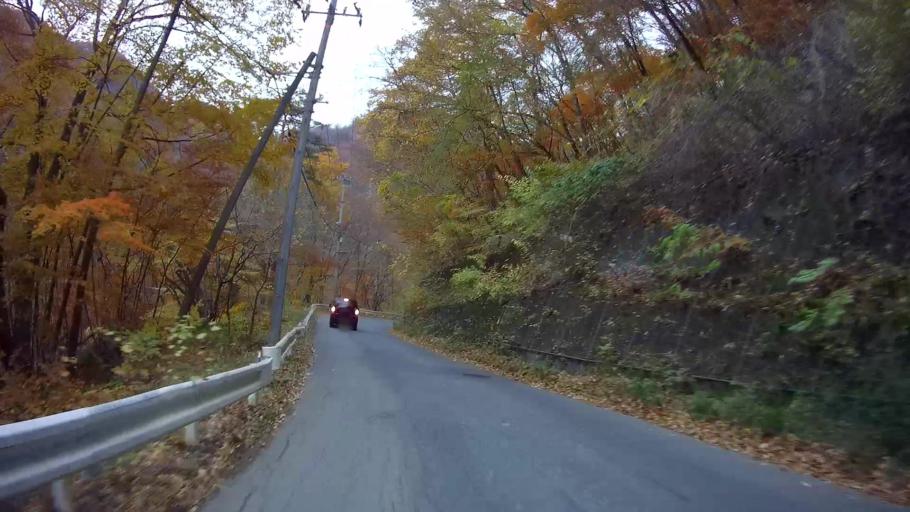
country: JP
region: Gunma
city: Nakanojomachi
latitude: 36.6246
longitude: 138.6465
